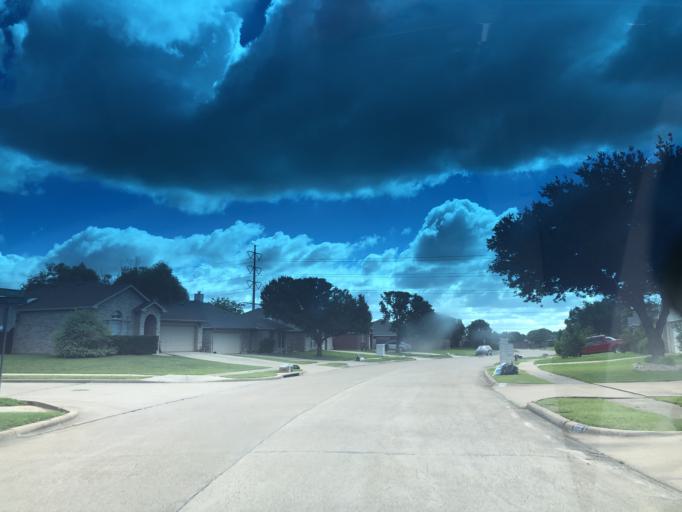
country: US
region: Texas
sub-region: Dallas County
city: Grand Prairie
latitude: 32.6957
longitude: -97.0365
